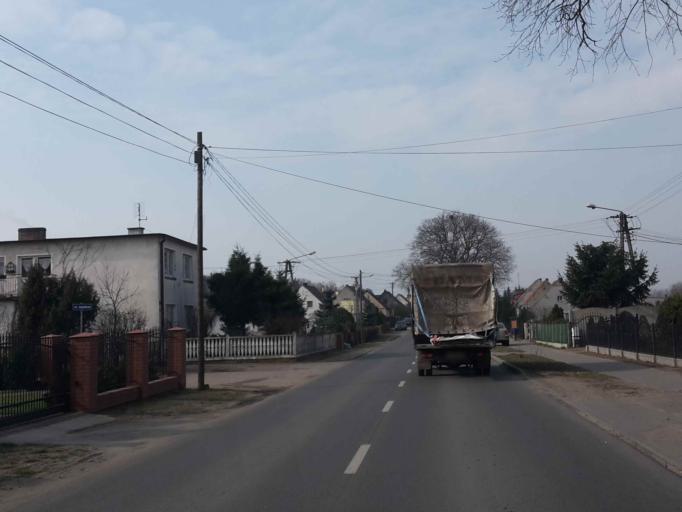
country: PL
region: Kujawsko-Pomorskie
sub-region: Powiat nakielski
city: Naklo nad Notecia
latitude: 53.1164
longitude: 17.5951
